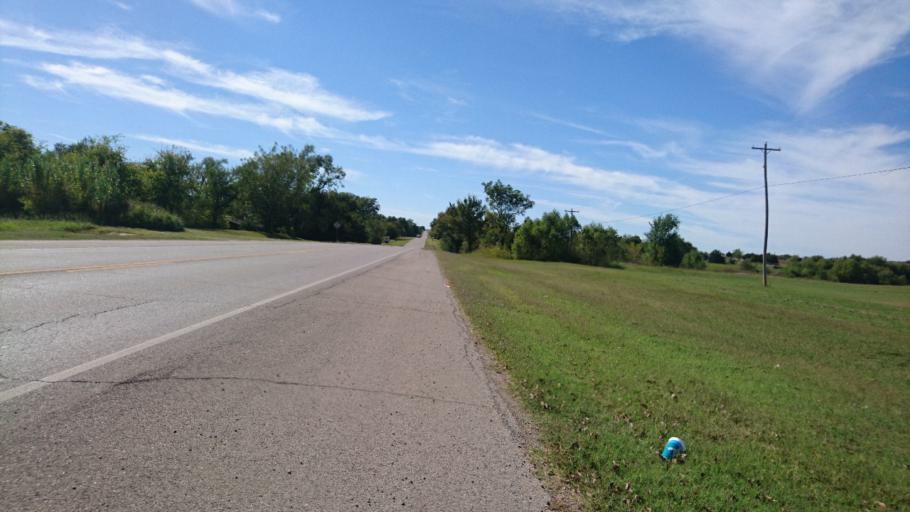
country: US
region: Oklahoma
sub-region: Lincoln County
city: Chandler
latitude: 35.7099
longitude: -96.7700
